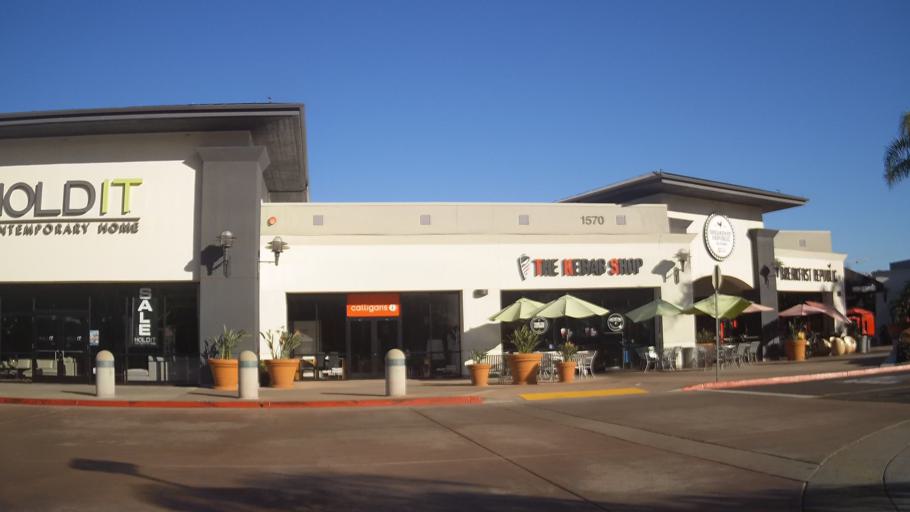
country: US
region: California
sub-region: San Diego County
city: San Diego
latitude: 32.7704
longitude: -117.1502
